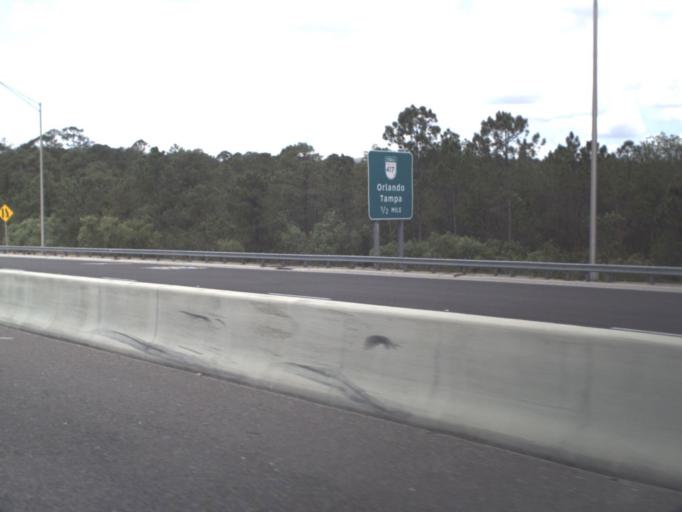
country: US
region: Florida
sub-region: Orange County
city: Alafaya
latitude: 28.4516
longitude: -81.2109
